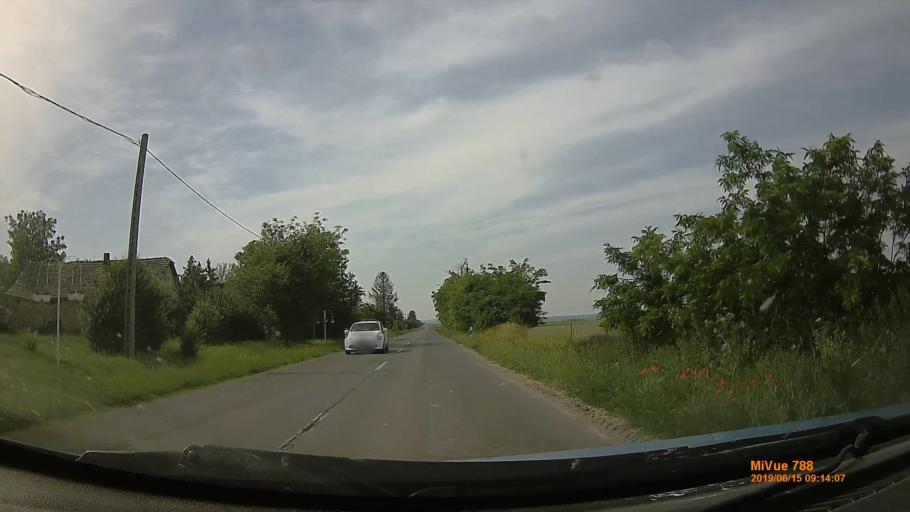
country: HU
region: Tolna
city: Iregszemcse
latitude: 46.6465
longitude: 18.1953
